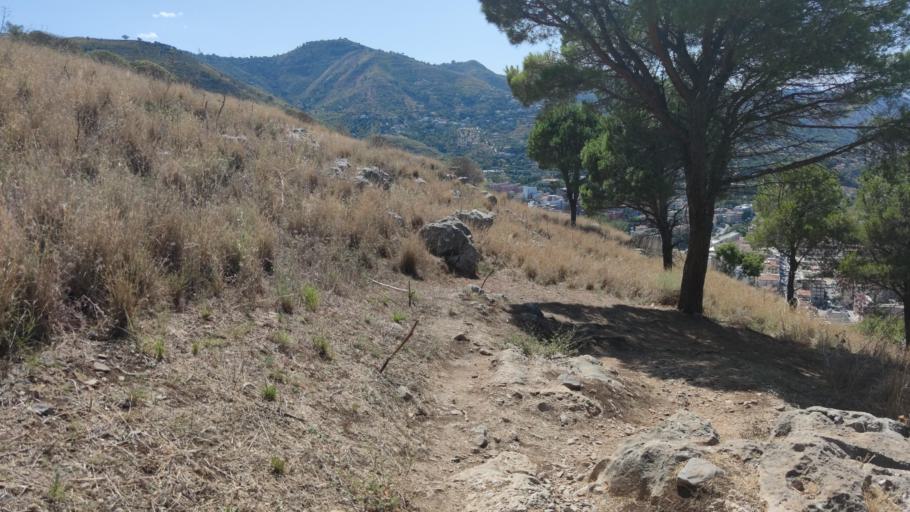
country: IT
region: Sicily
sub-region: Palermo
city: Cefalu
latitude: 38.0363
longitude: 14.0257
